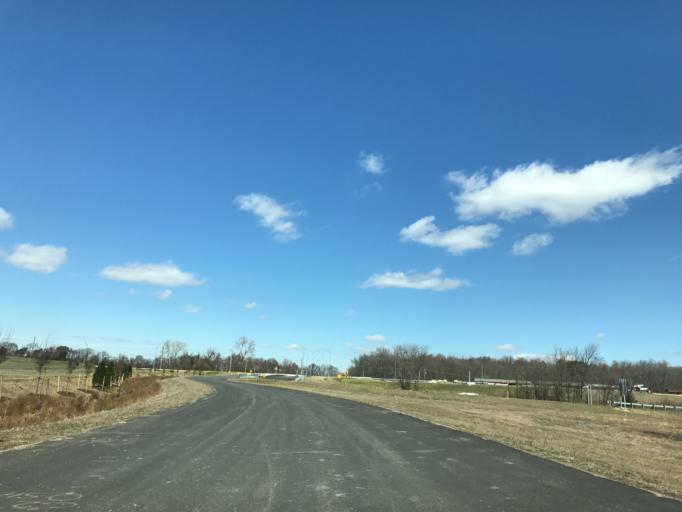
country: US
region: Maryland
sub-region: Queen Anne's County
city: Centreville
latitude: 39.0256
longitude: -76.0296
